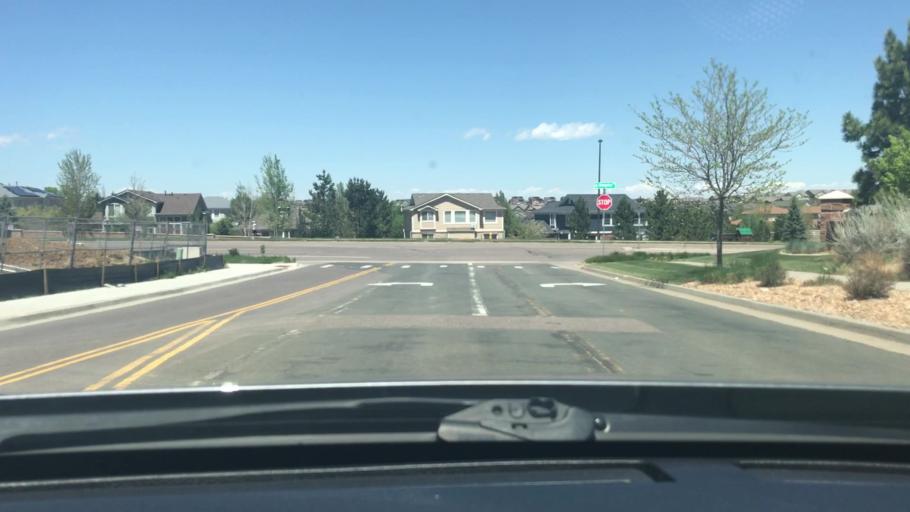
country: US
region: Colorado
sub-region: Arapahoe County
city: Dove Valley
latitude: 39.6524
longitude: -104.7438
